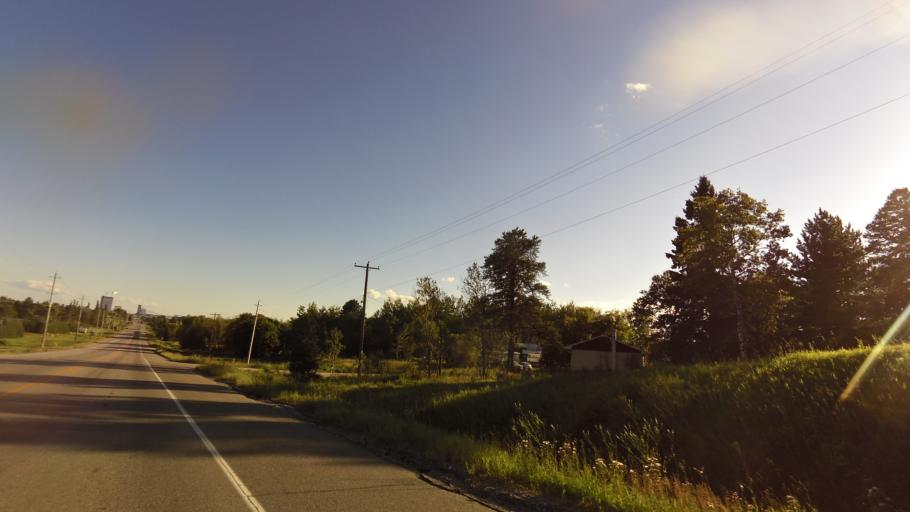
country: CA
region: Ontario
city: Dryden
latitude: 49.8085
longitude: -92.8474
